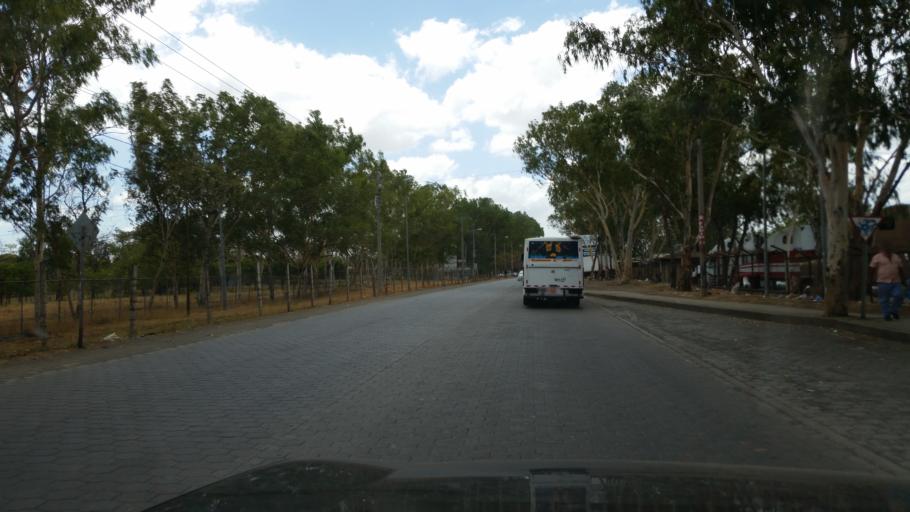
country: NI
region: Managua
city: Managua
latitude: 12.1447
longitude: -86.1953
